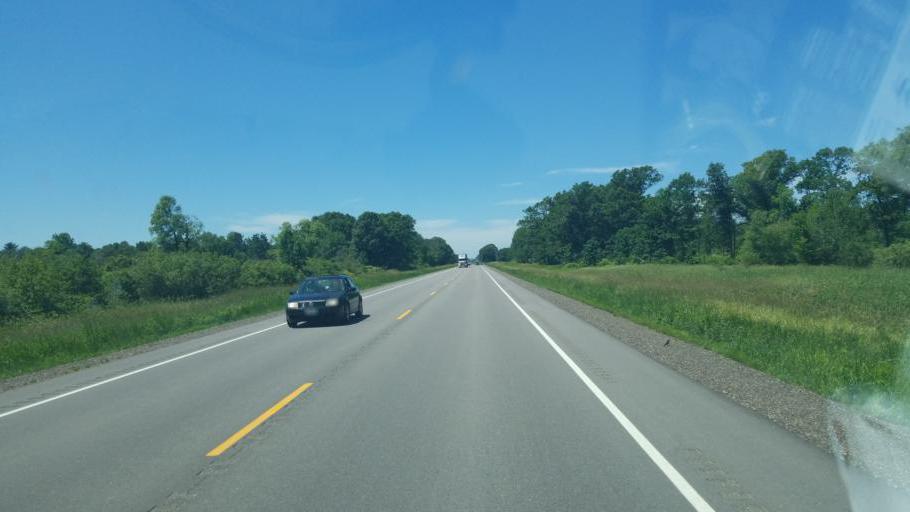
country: US
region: Wisconsin
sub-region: Juneau County
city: New Lisbon
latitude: 44.0258
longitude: -90.2606
